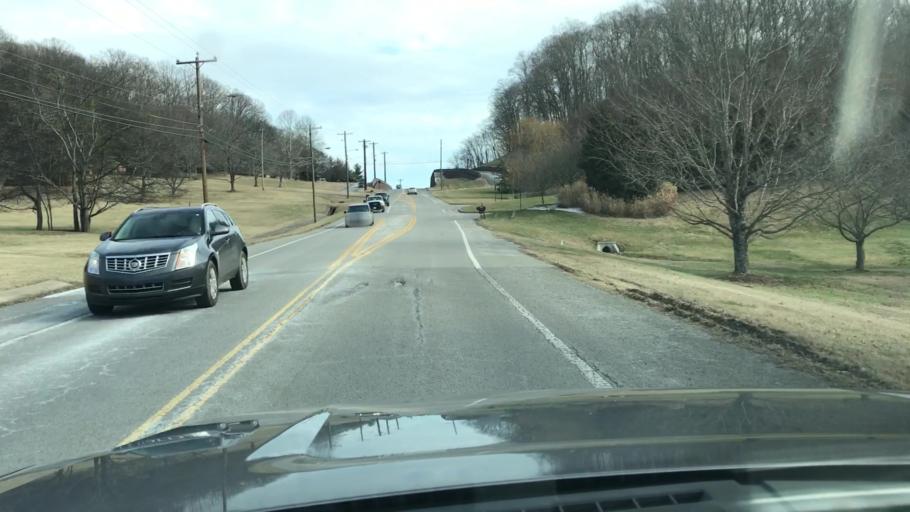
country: US
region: Tennessee
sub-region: Williamson County
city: Brentwood
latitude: 36.0129
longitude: -86.8340
